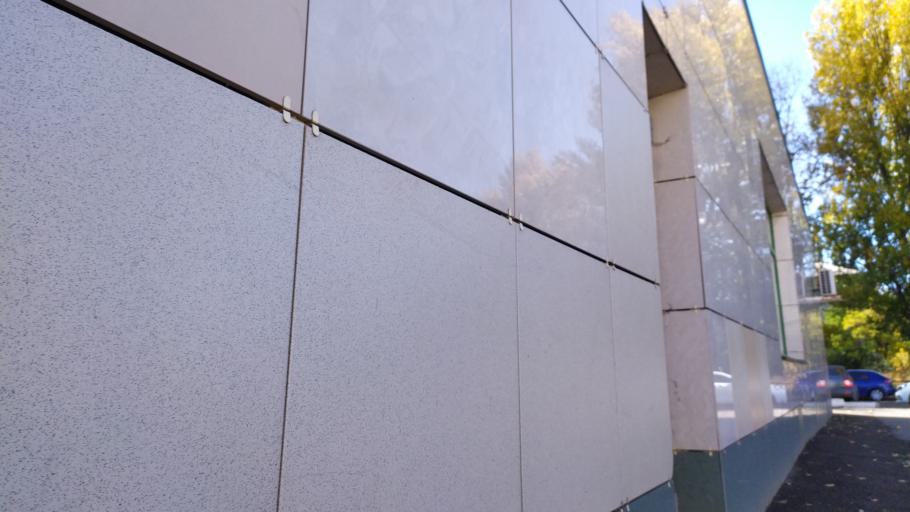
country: RU
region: Kursk
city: Kursk
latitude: 51.6515
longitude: 36.1401
